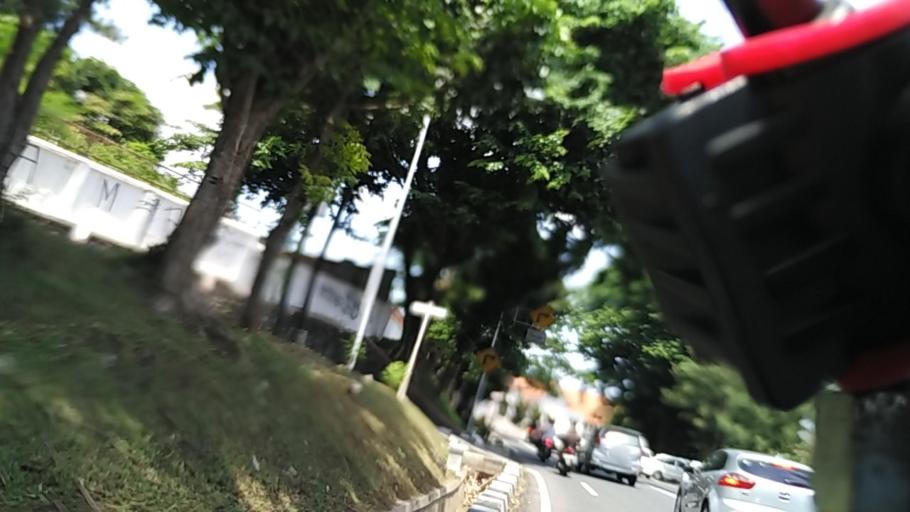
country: ID
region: Central Java
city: Semarang
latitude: -6.9984
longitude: 110.4058
